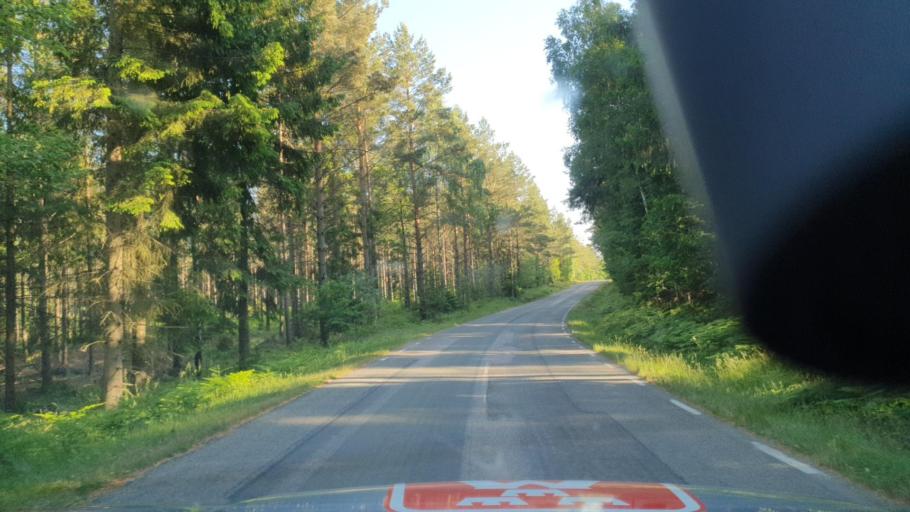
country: SE
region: Kalmar
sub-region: Torsas Kommun
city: Torsas
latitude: 56.4846
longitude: 16.0955
